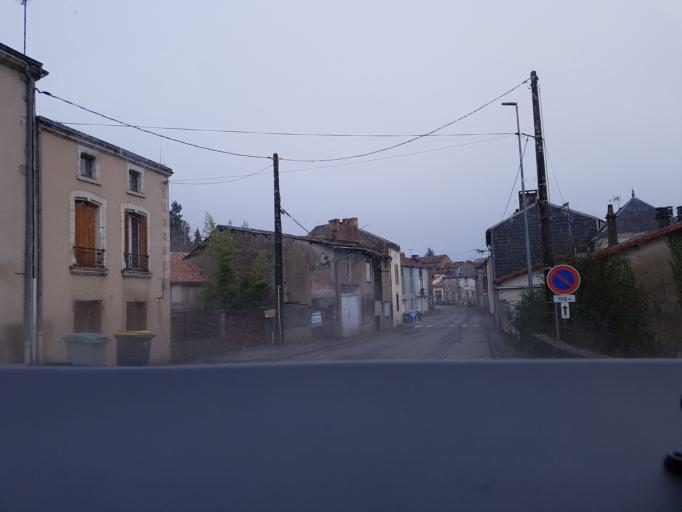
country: FR
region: Poitou-Charentes
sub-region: Departement des Deux-Sevres
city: Parthenay
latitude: 46.6533
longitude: -0.2480
